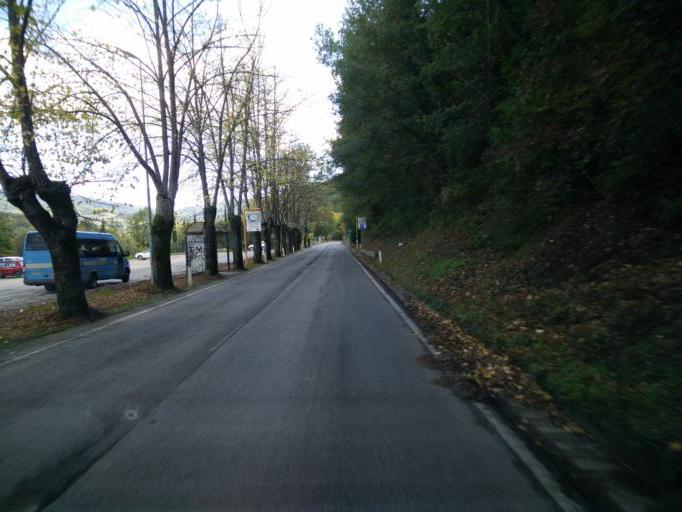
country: IT
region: Tuscany
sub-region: Province of Florence
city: Greve in Chianti
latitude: 43.5732
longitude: 11.3189
